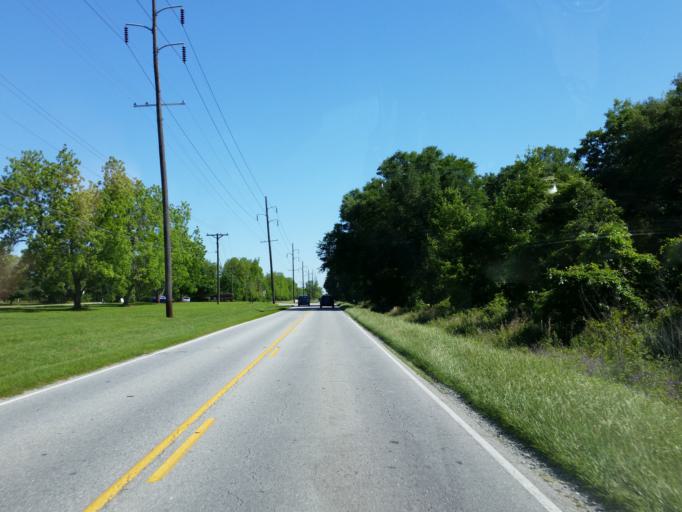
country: US
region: Georgia
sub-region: Lowndes County
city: Hahira
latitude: 30.9222
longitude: -83.3495
